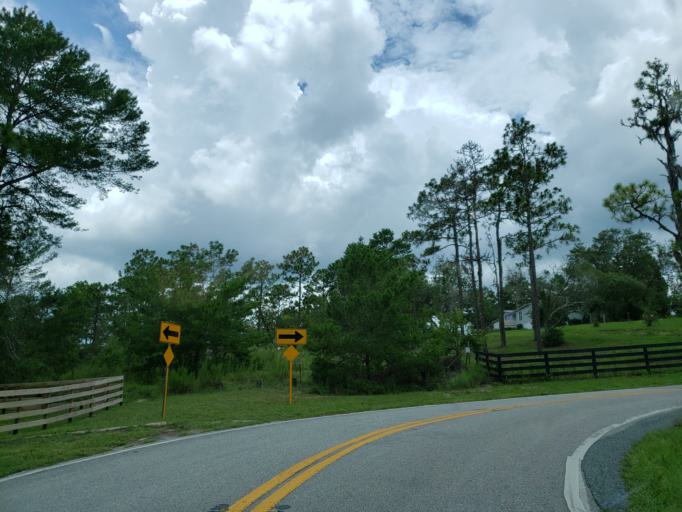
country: US
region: Florida
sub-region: Citrus County
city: Floral City
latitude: 28.6668
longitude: -82.3184
